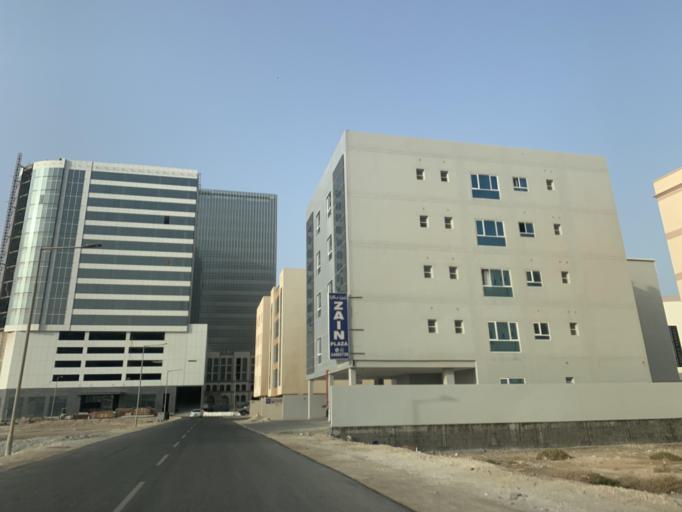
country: BH
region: Manama
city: Jidd Hafs
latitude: 26.2416
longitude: 50.5303
